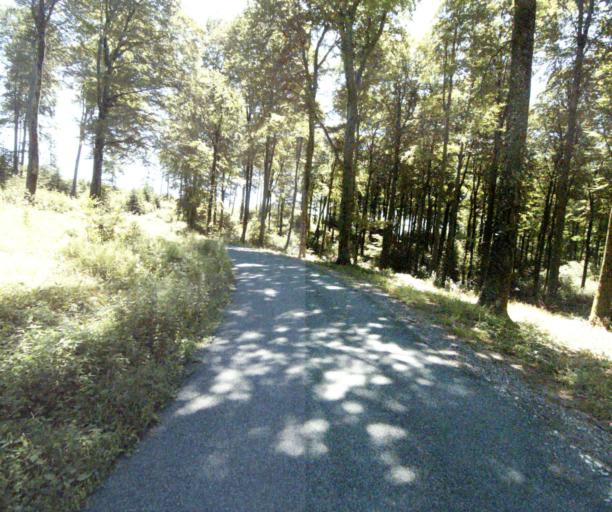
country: FR
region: Midi-Pyrenees
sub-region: Departement du Tarn
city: Dourgne
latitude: 43.4124
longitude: 2.1880
